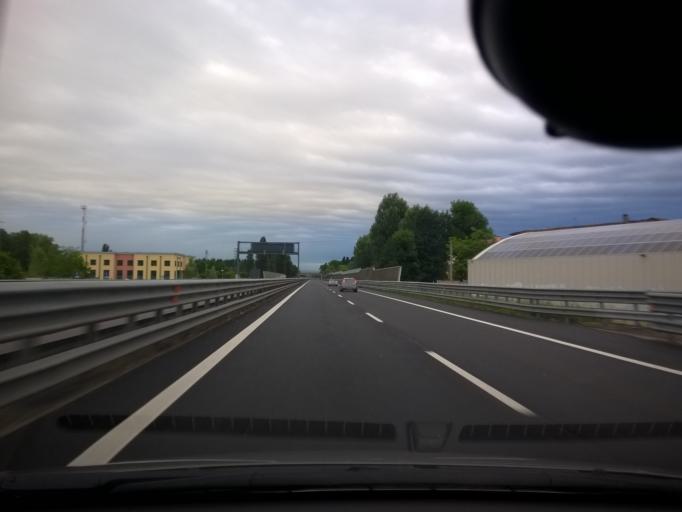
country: IT
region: Veneto
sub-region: Provincia di Venezia
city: Marcon-Gaggio-Colmello
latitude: 45.5531
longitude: 12.3104
